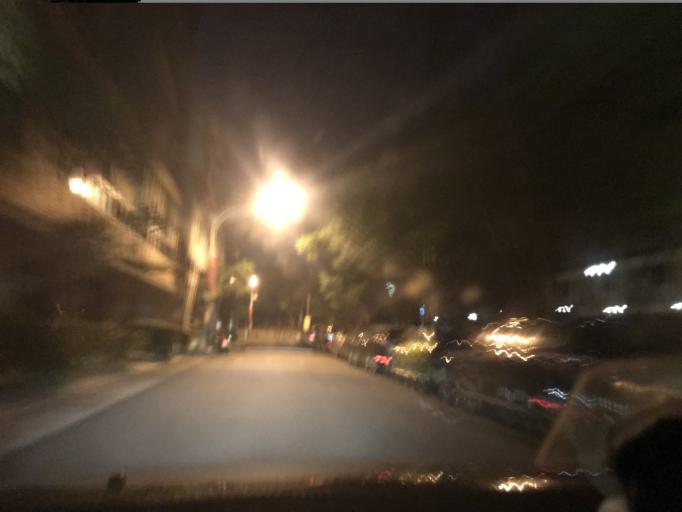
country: TW
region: Taiwan
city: Taoyuan City
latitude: 24.9776
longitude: 121.2336
